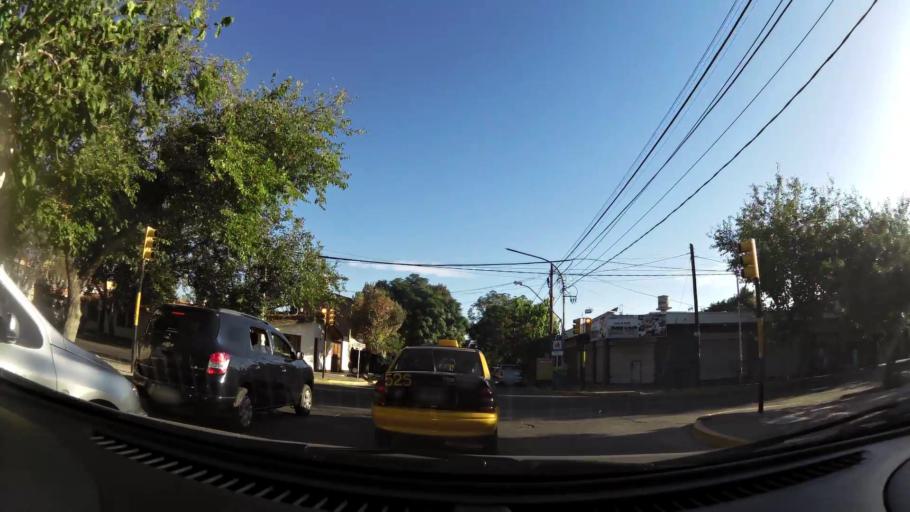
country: AR
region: Mendoza
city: Las Heras
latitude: -32.8689
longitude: -68.8273
